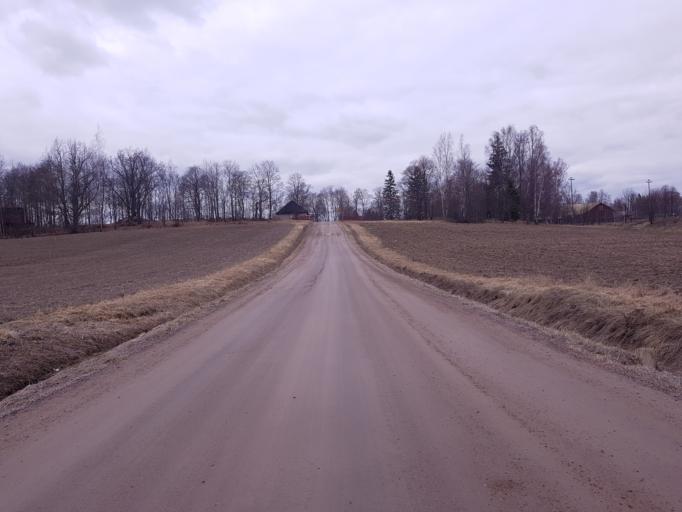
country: FI
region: Uusimaa
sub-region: Helsinki
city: Kilo
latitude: 60.2633
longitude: 24.7854
